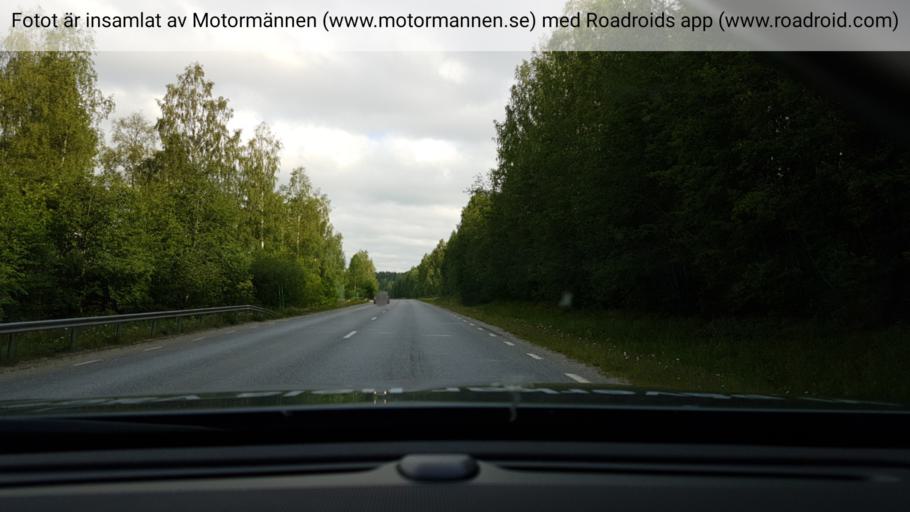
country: SE
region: Vaesterbotten
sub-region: Vindelns Kommun
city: Vindeln
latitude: 64.3014
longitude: 19.6154
